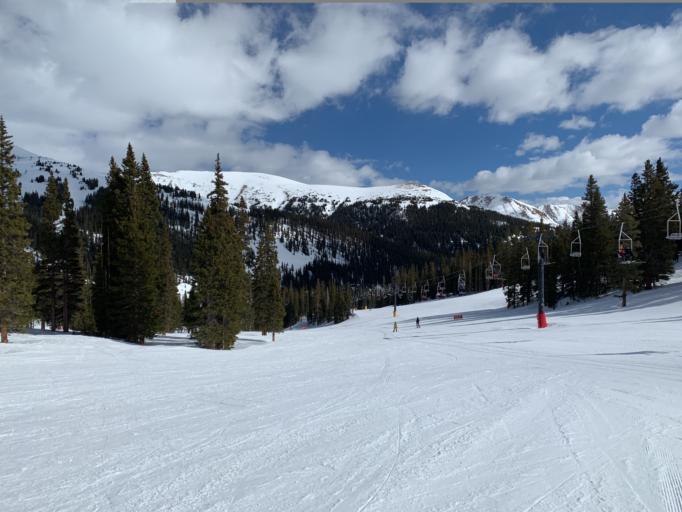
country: US
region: Colorado
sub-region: Summit County
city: Keystone
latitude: 39.6730
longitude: -105.9057
